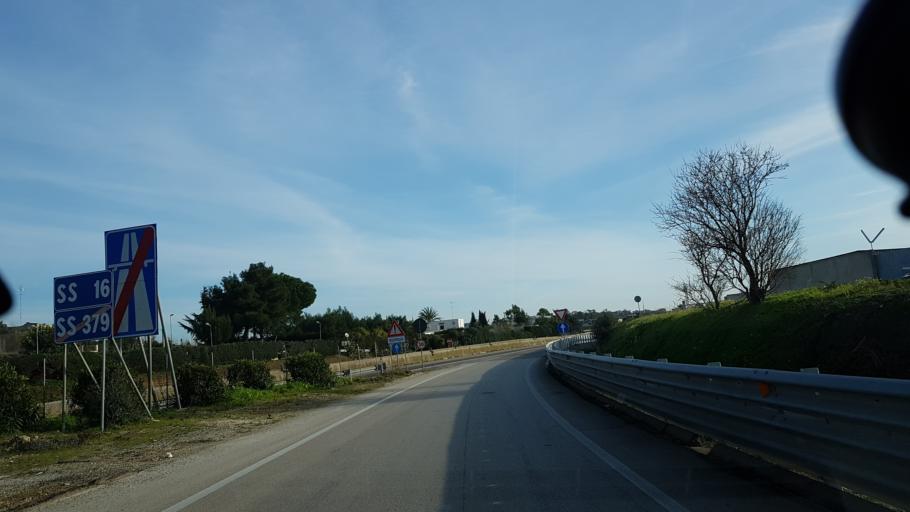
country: IT
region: Apulia
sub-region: Provincia di Brindisi
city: Brindisi
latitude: 40.6418
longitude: 17.9142
